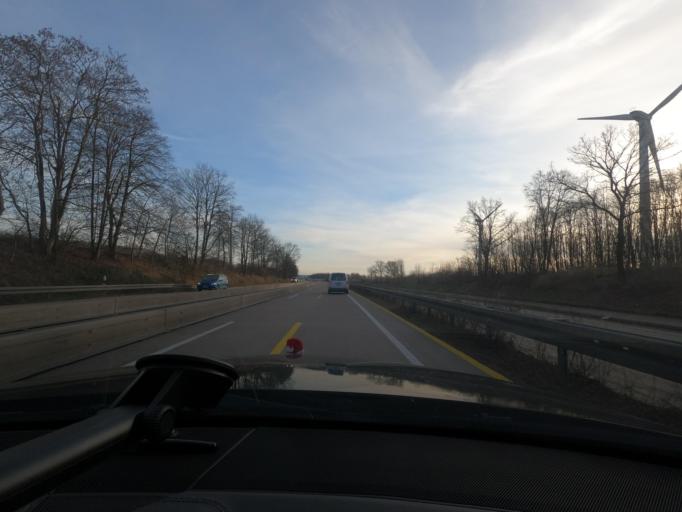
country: DE
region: Lower Saxony
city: Harsum
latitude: 52.2044
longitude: 9.9372
